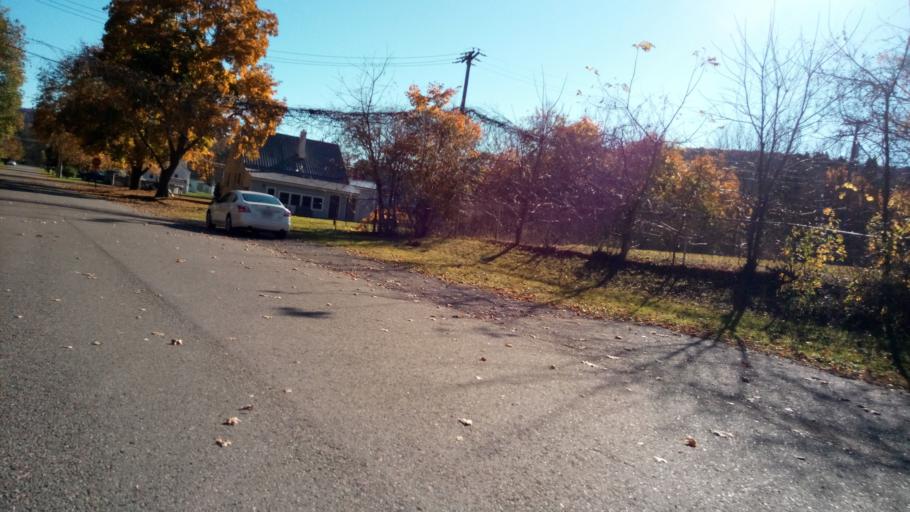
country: US
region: New York
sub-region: Chemung County
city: Southport
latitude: 42.0705
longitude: -76.8183
